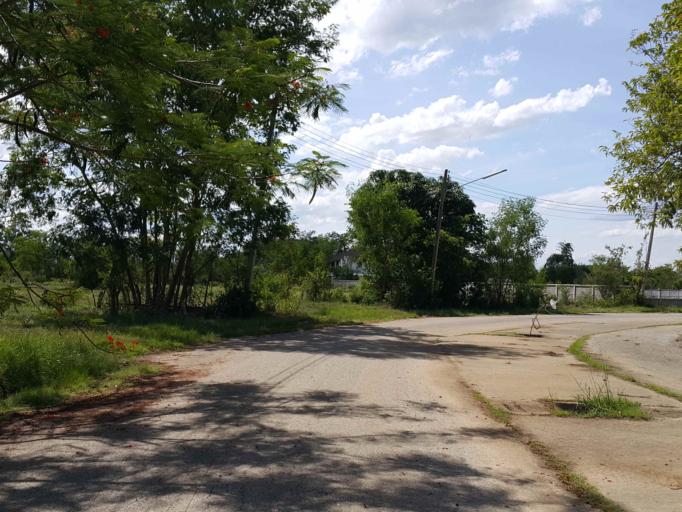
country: TH
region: Chiang Mai
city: San Kamphaeng
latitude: 18.7583
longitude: 99.1094
